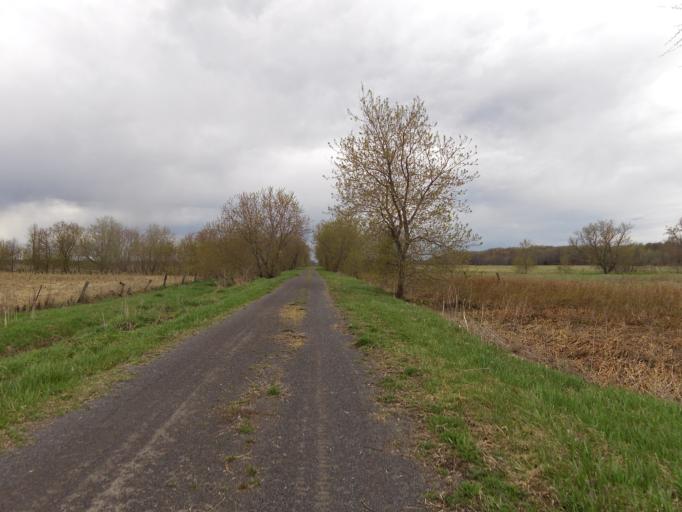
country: CA
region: Quebec
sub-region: Outaouais
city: Papineauville
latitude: 45.5229
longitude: -74.9092
